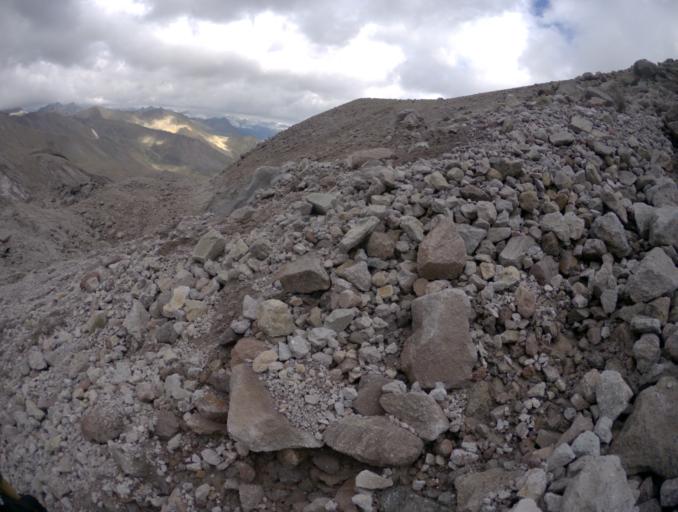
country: RU
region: Kabardino-Balkariya
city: Terskol
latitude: 43.3807
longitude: 42.3950
